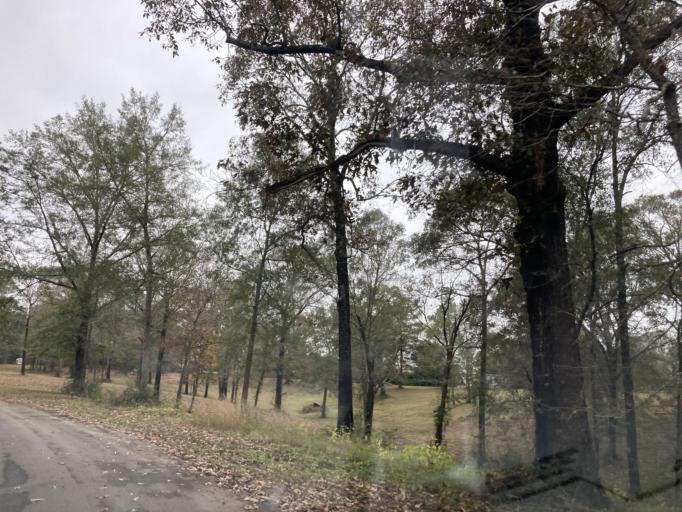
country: US
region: Mississippi
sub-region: Lamar County
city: Purvis
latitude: 31.1864
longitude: -89.4117
